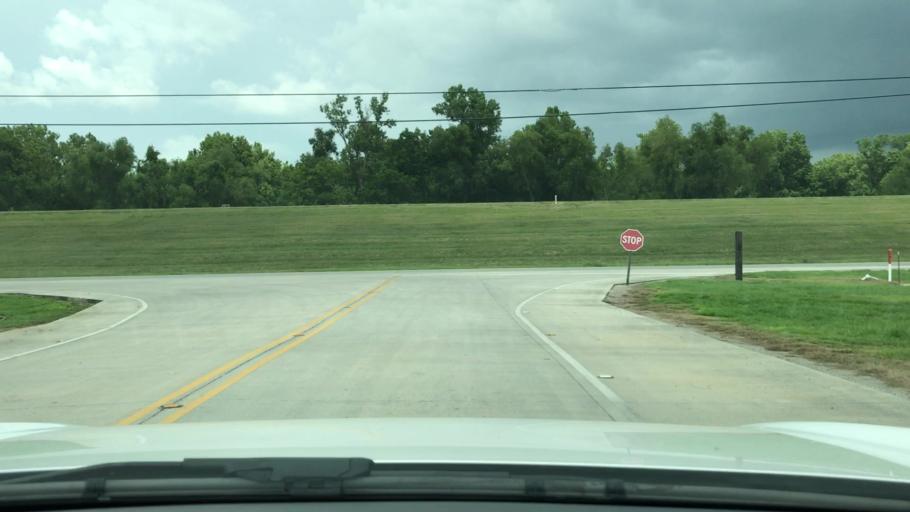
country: US
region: Louisiana
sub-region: Iberville Parish
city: Saint Gabriel
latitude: 30.2706
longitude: -91.1470
